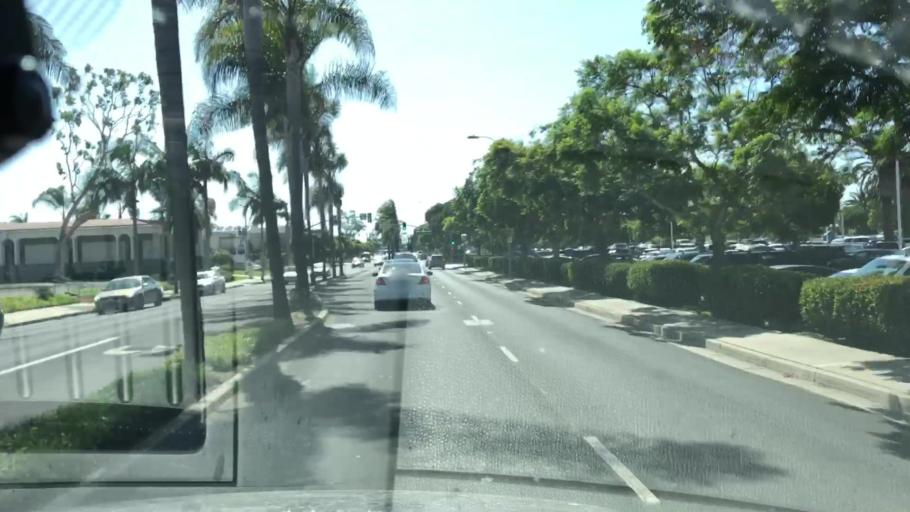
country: US
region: California
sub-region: Ventura County
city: Ventura
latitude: 34.2684
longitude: -119.2468
